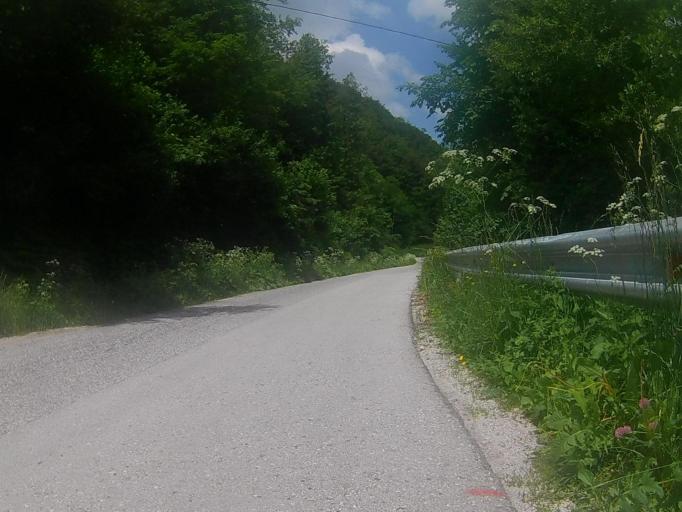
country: SI
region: Maribor
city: Bresternica
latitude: 46.5965
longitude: 15.5553
